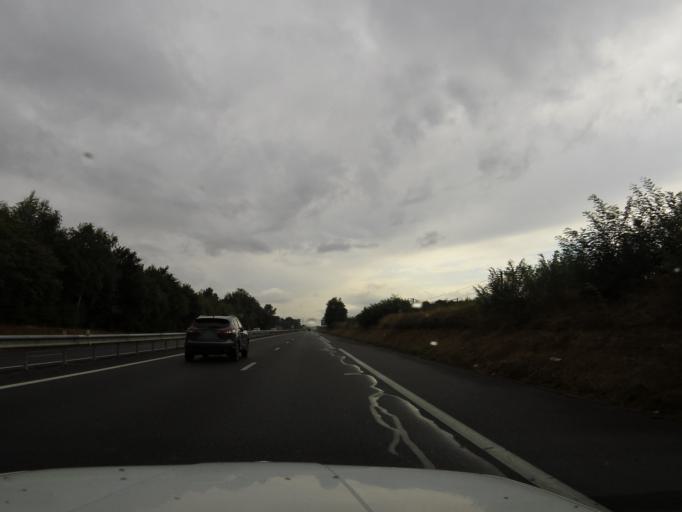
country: FR
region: Rhone-Alpes
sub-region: Departement du Rhone
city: Jons
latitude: 45.7824
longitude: 5.0815
